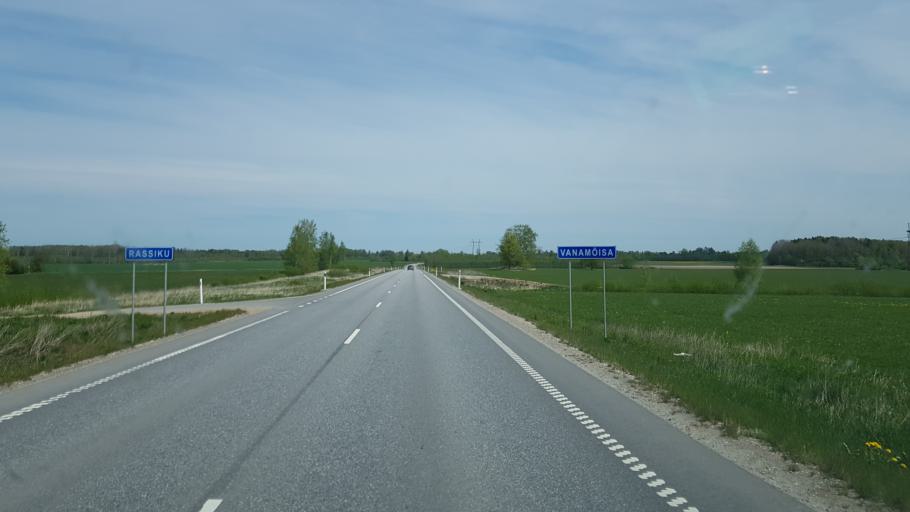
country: EE
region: Jogevamaa
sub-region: Mustvee linn
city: Mustvee
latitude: 58.8240
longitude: 26.7504
